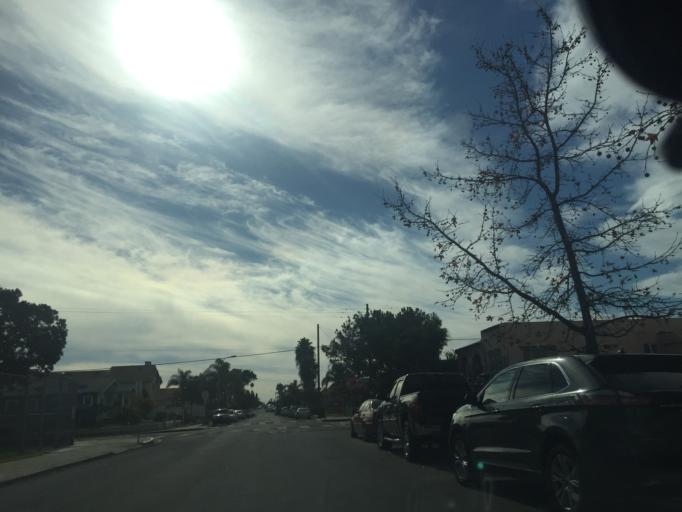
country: US
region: California
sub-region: San Diego County
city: Lemon Grove
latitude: 32.7519
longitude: -117.0944
